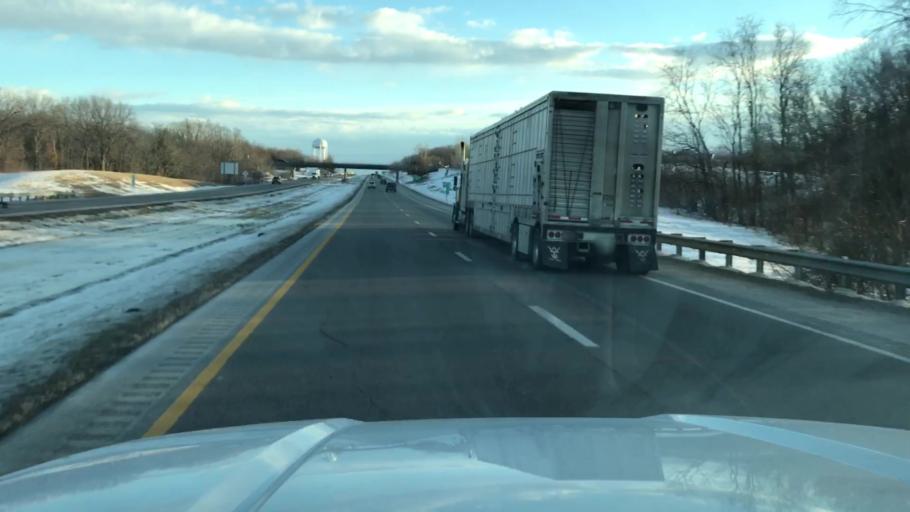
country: US
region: Missouri
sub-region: Andrew County
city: Country Club Village
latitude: 39.8096
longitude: -94.8021
